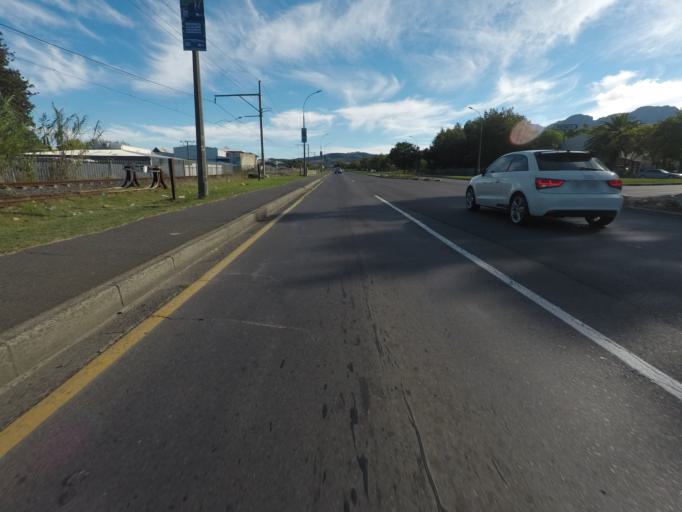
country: ZA
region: Western Cape
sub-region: Cape Winelands District Municipality
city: Stellenbosch
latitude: -33.9303
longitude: 18.8535
